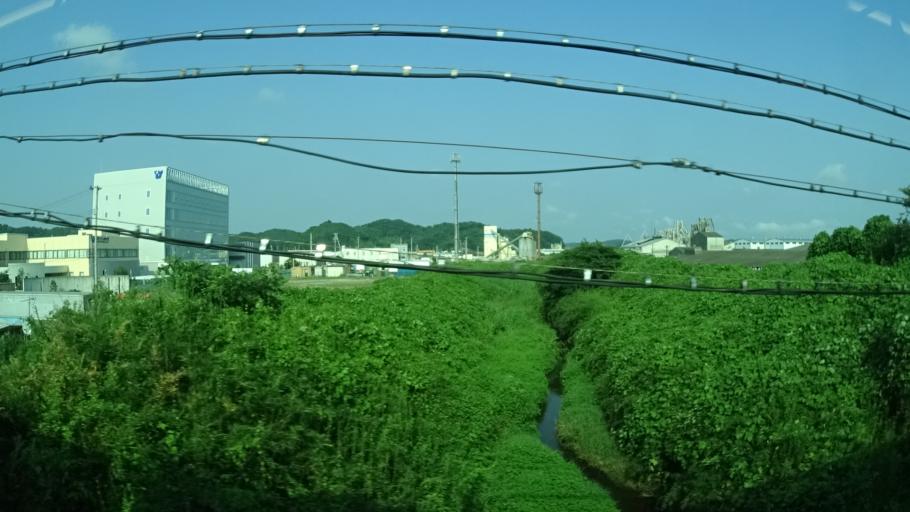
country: JP
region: Fukushima
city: Iwaki
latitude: 36.9836
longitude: 140.8632
